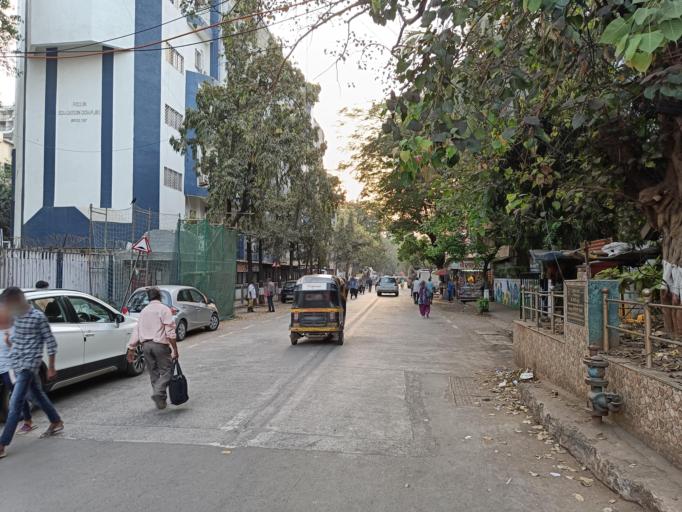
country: IN
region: Maharashtra
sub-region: Mumbai Suburban
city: Mumbai
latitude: 19.0813
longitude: 72.8377
